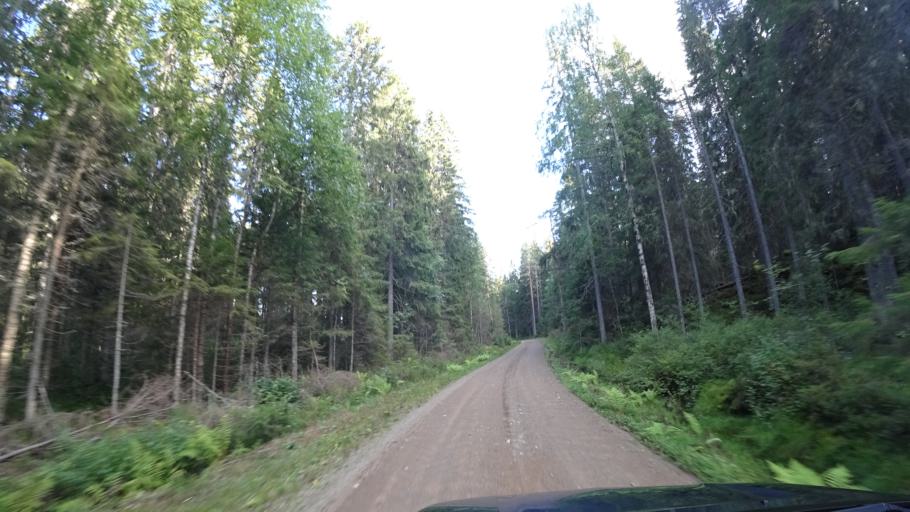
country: FI
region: Paijanne Tavastia
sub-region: Lahti
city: Auttoinen
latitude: 61.2212
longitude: 25.2026
